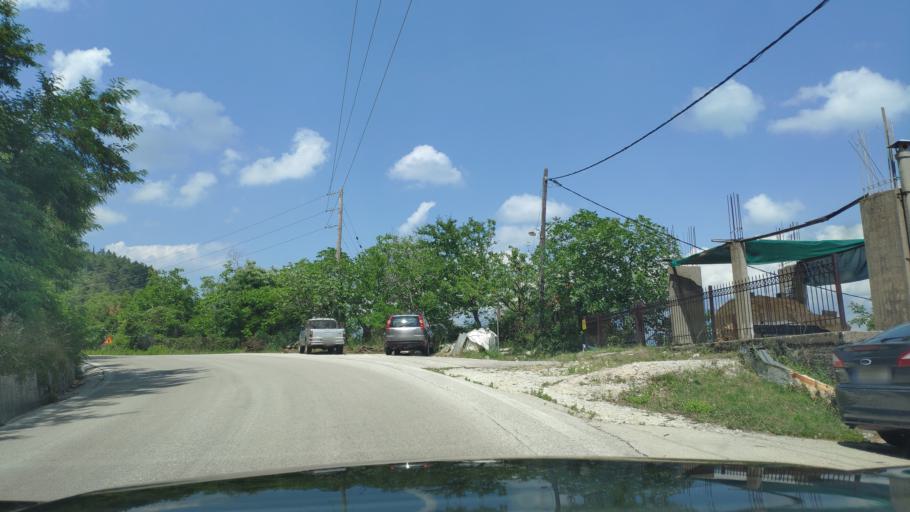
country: GR
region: Epirus
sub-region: Nomos Artas
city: Agios Dimitrios
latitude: 39.3232
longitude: 20.9950
